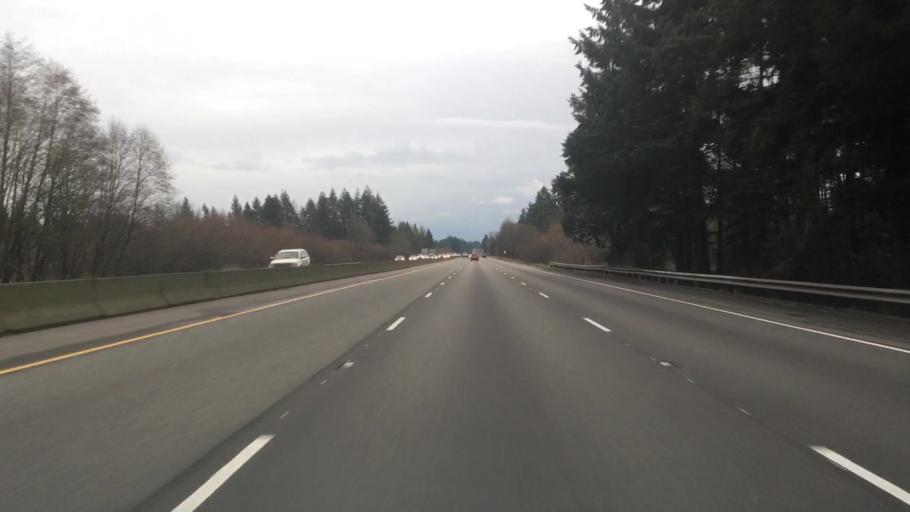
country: US
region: Washington
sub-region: Thurston County
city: Tumwater
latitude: 46.9404
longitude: -122.9413
